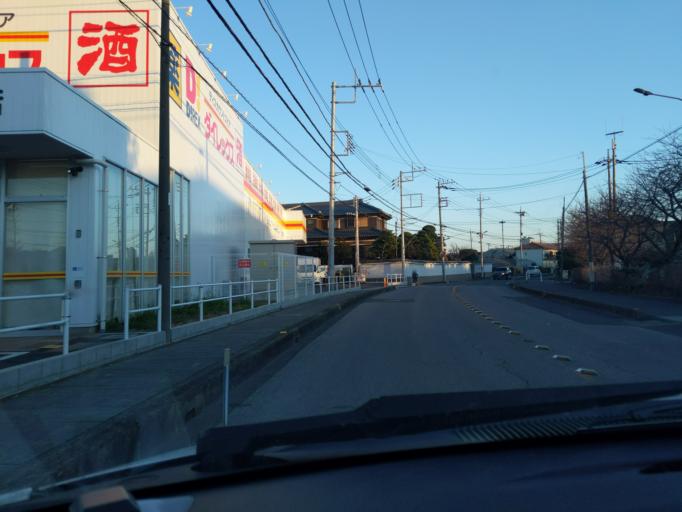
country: JP
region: Saitama
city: Koshigaya
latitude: 35.8543
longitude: 139.7863
